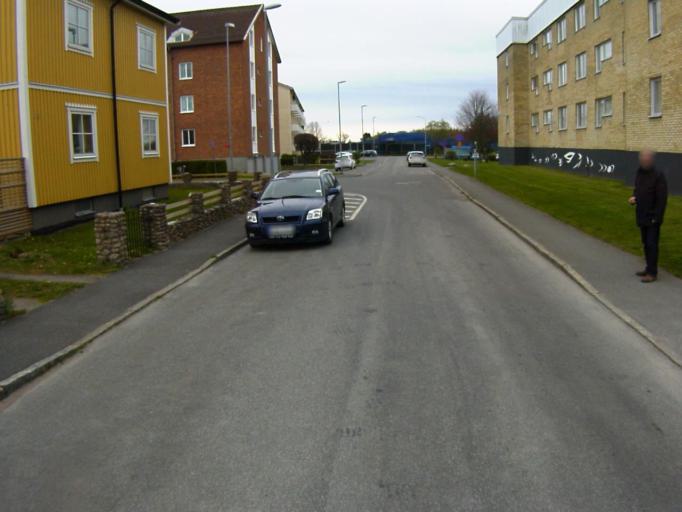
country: SE
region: Skane
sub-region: Kristianstads Kommun
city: Kristianstad
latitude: 56.0183
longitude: 14.1422
